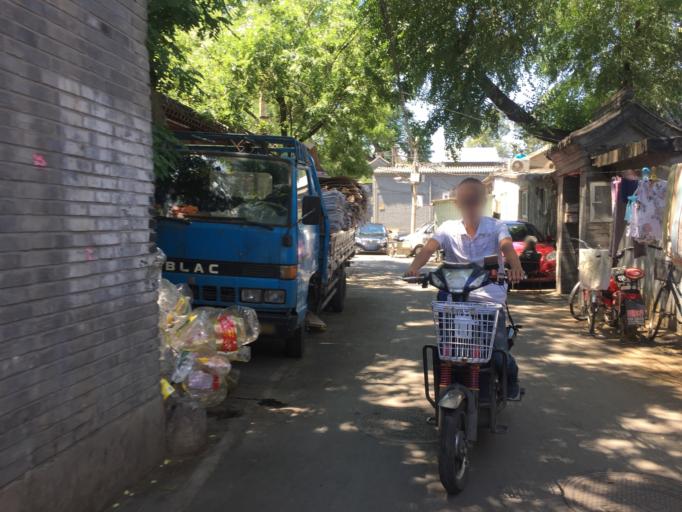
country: CN
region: Beijing
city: Jingshan
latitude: 39.9276
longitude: 116.3874
